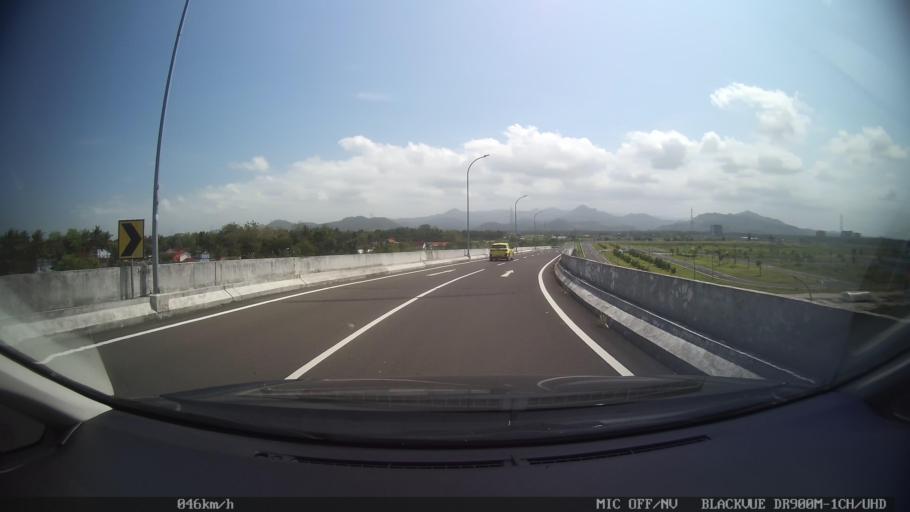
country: ID
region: Daerah Istimewa Yogyakarta
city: Srandakan
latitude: -7.8966
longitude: 110.0572
